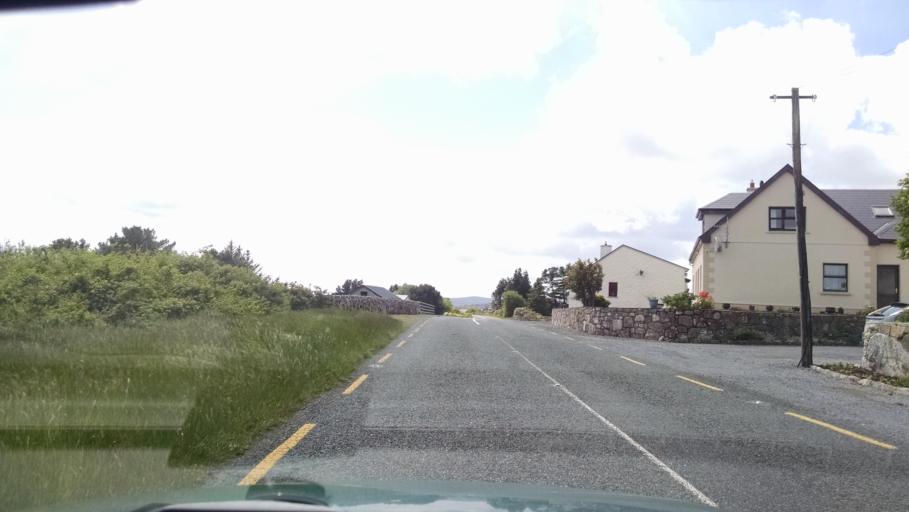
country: IE
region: Connaught
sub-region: County Galway
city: Oughterard
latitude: 53.3834
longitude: -9.6639
